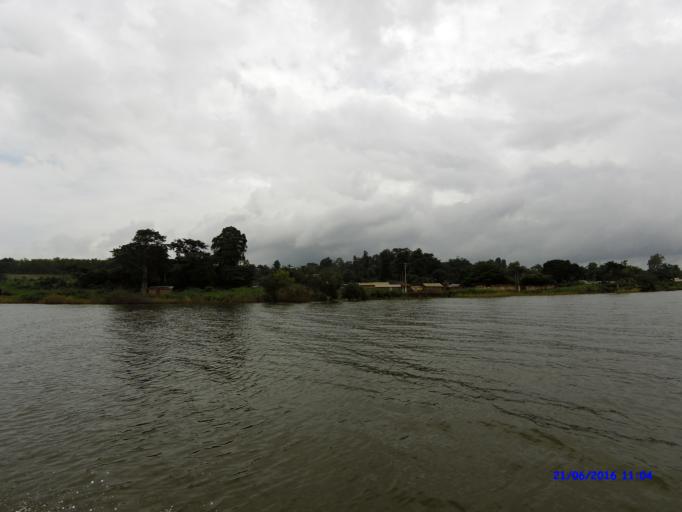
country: BJ
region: Mono
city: Come
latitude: 6.5140
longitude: 1.9680
